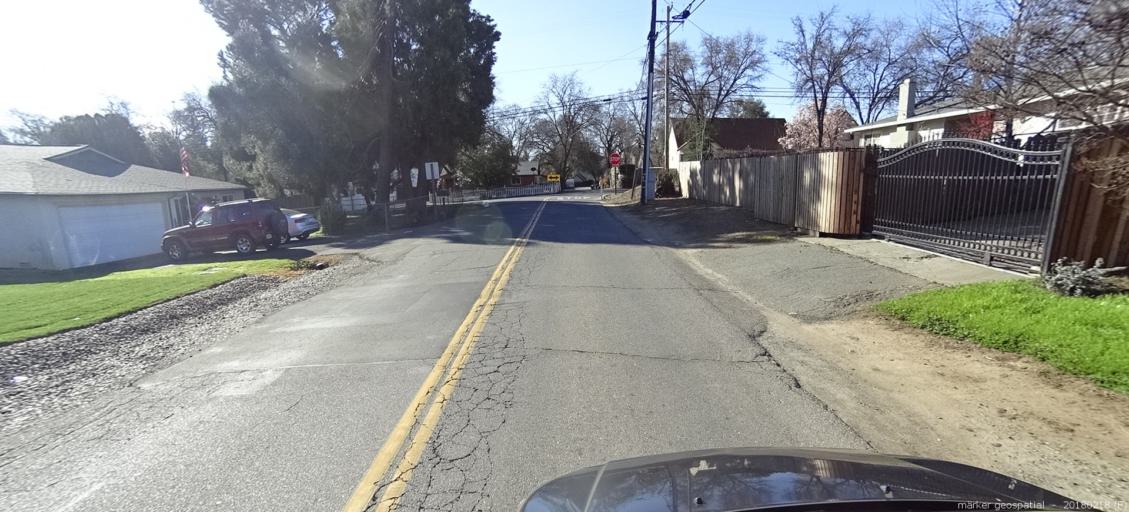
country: US
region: California
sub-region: Sacramento County
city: Orangevale
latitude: 38.6700
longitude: -121.2397
